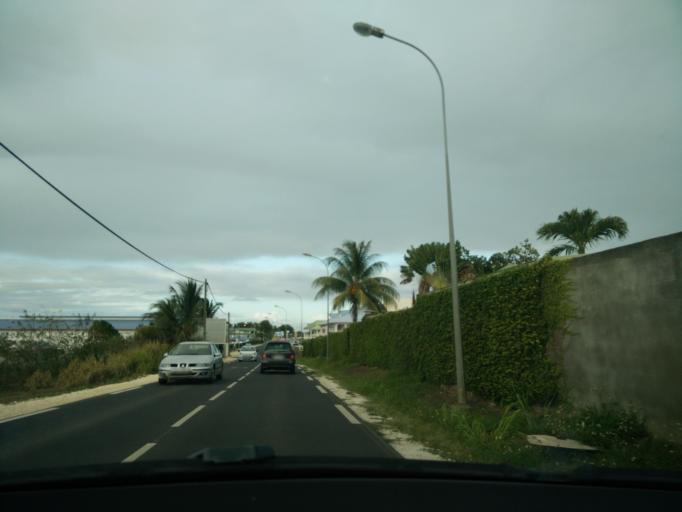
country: GP
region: Guadeloupe
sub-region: Guadeloupe
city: Baie-Mahault
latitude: 16.2410
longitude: -61.5984
